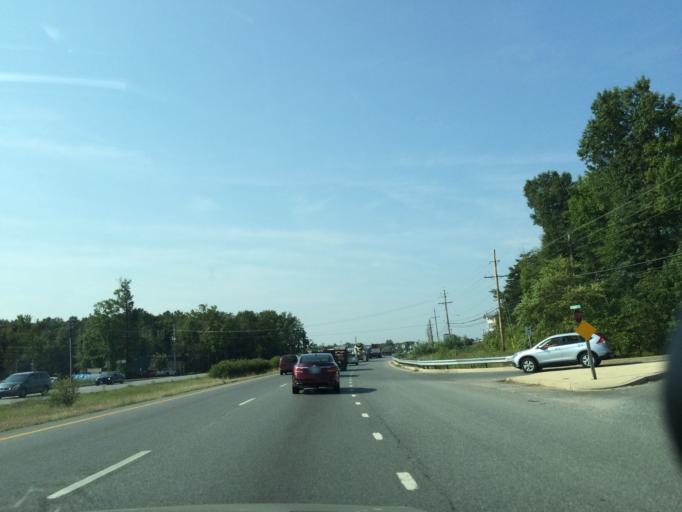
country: US
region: Maryland
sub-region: Charles County
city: Saint Charles
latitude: 38.5953
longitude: -76.9385
